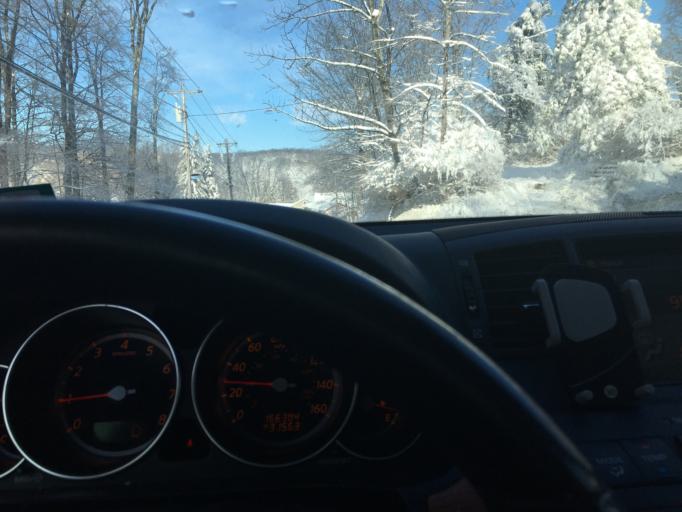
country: US
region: New Jersey
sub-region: Sussex County
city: Highland Lake
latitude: 41.1780
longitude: -74.4552
